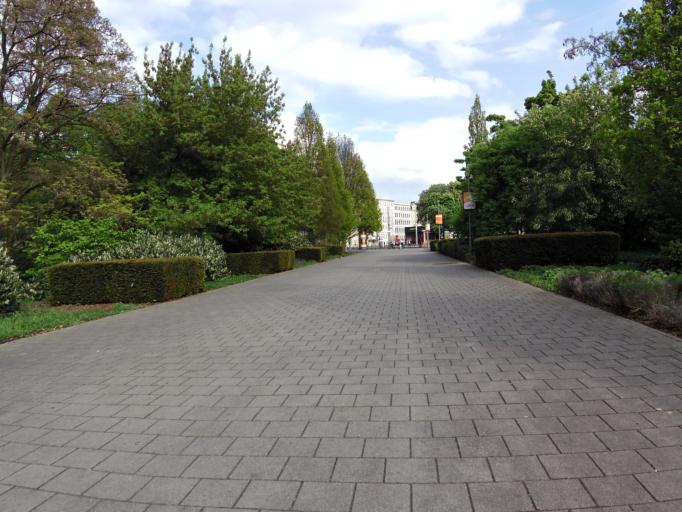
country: DE
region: Saxony
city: Leipzig
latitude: 51.3424
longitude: 12.3563
